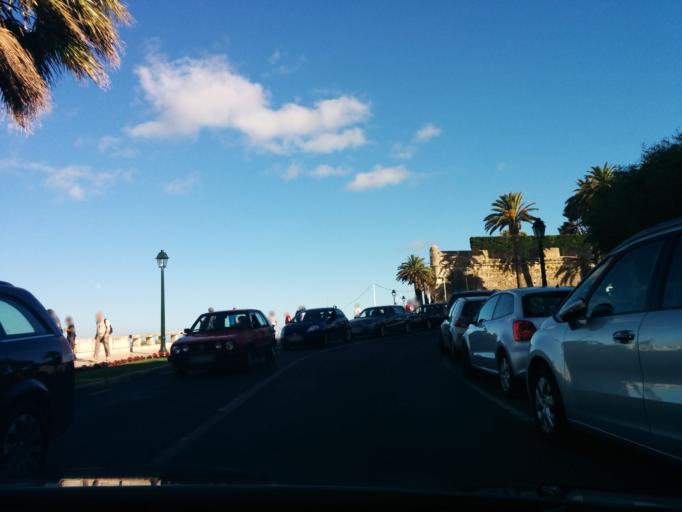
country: PT
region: Lisbon
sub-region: Cascais
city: Cascais
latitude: 38.6956
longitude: -9.4196
